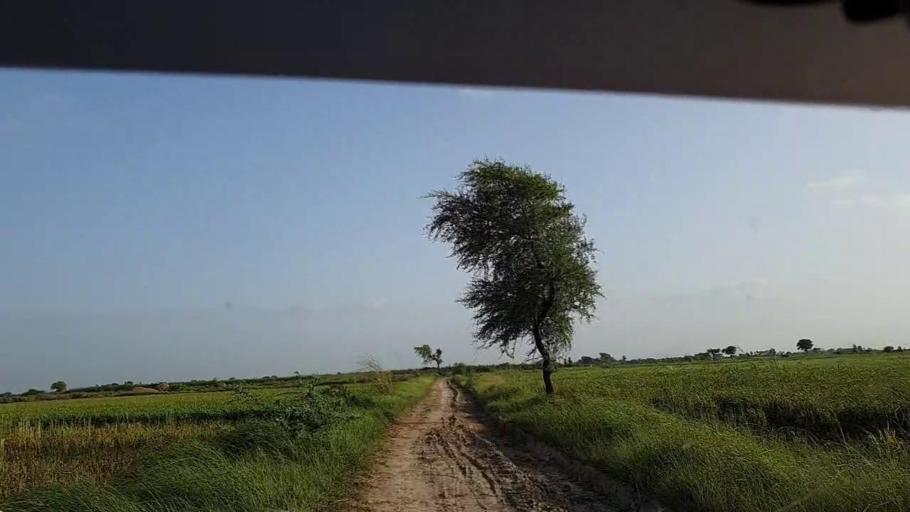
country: PK
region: Sindh
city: Badin
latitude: 24.5610
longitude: 68.8626
